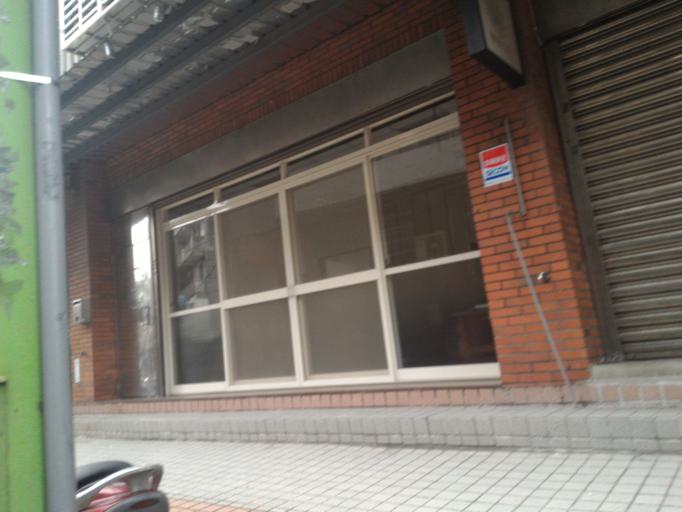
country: TW
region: Taipei
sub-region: Taipei
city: Banqiao
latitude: 25.0393
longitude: 121.4568
